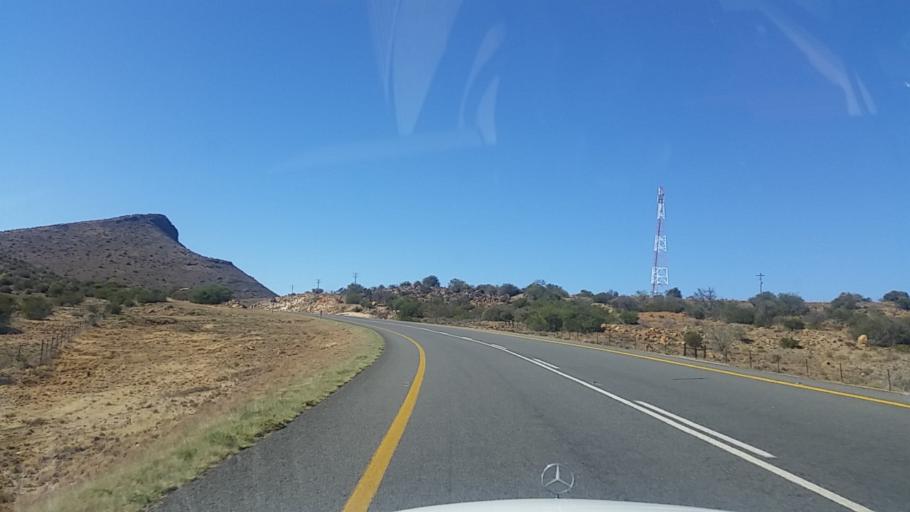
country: ZA
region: Eastern Cape
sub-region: Cacadu District Municipality
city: Graaff-Reinet
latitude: -32.1057
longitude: 24.6063
